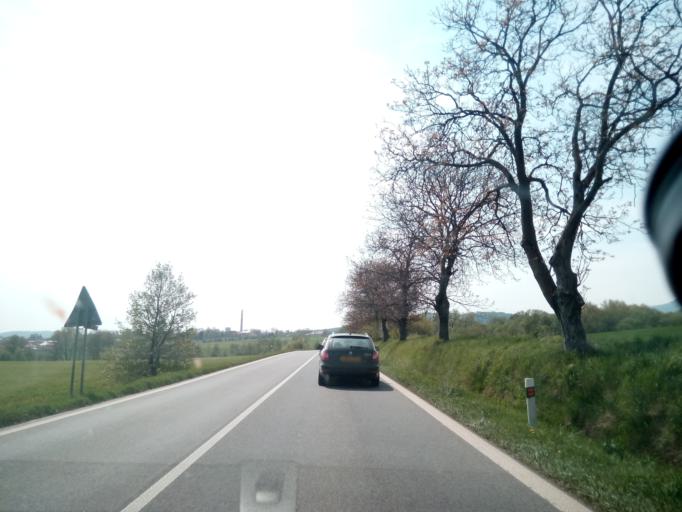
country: SK
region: Presovsky
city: Giraltovce
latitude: 49.0173
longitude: 21.5334
